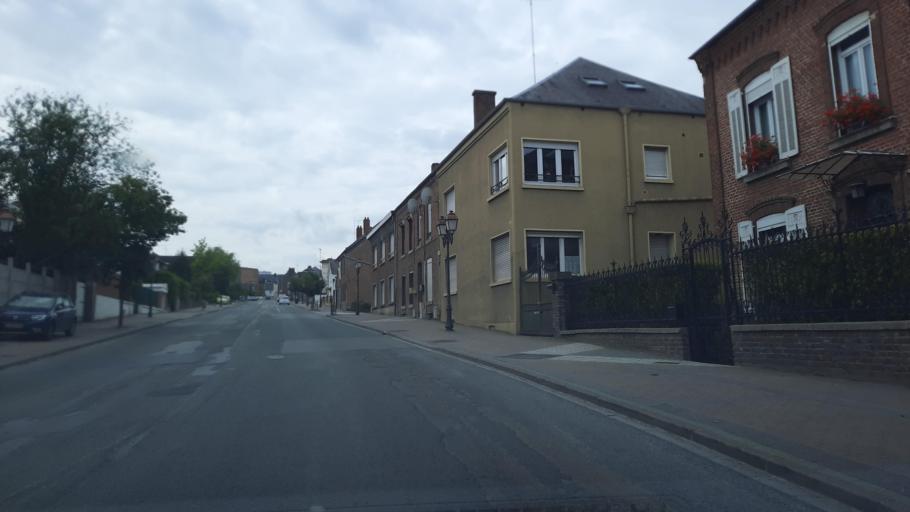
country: FR
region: Nord-Pas-de-Calais
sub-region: Departement du Nord
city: Avesnes-sur-Helpe
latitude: 50.1244
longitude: 3.9257
